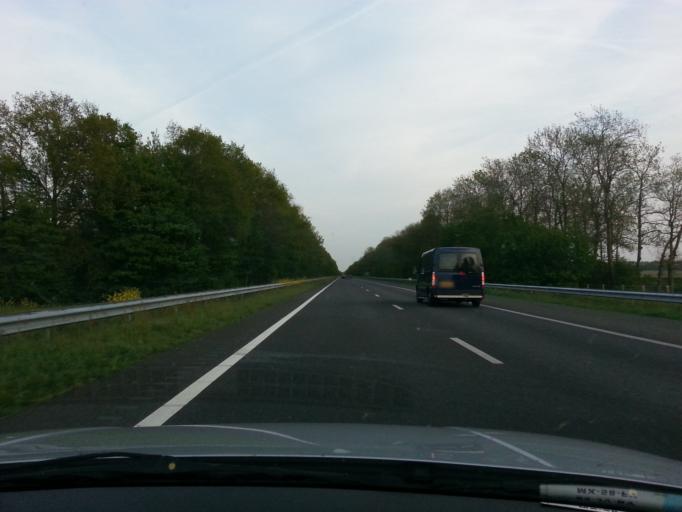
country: NL
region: Friesland
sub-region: Gemeente Lemsterland
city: Lemmer
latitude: 52.8044
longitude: 5.7485
